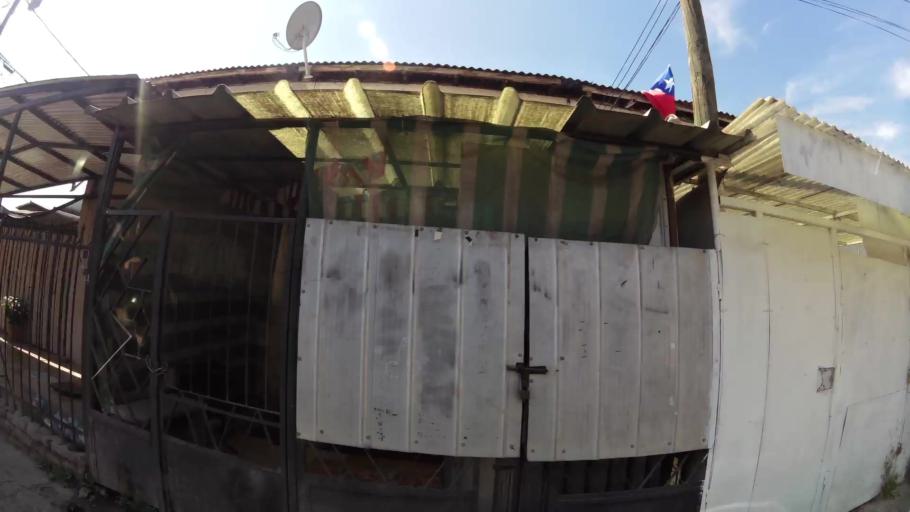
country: CL
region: Santiago Metropolitan
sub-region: Provincia de Santiago
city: La Pintana
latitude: -33.5620
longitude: -70.6372
